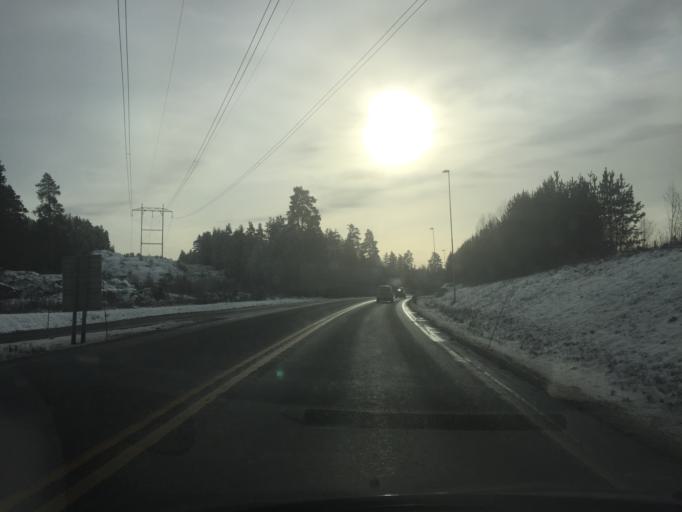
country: NO
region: Hedmark
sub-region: Loten
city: Loten
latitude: 60.7817
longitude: 11.3071
